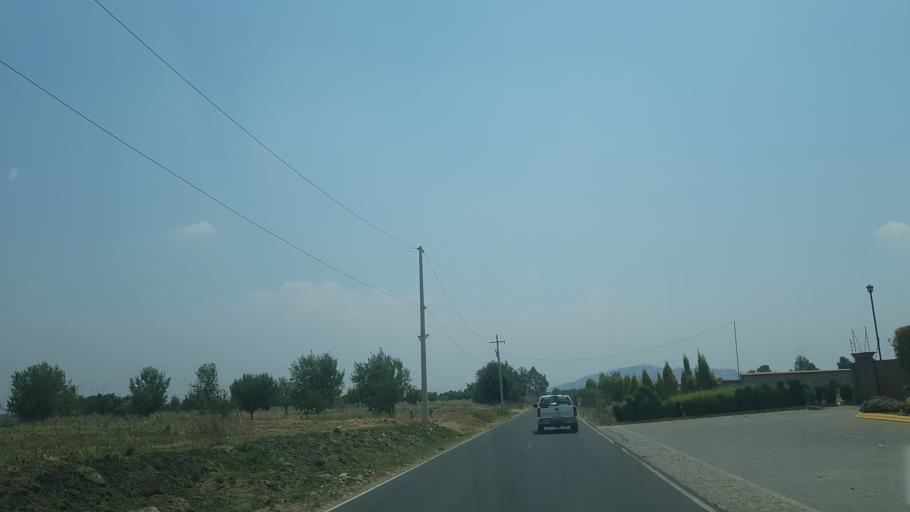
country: MX
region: Puebla
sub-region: San Jeronimo Tecuanipan
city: San Miguel Papaxtla
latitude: 19.0952
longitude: -98.4060
